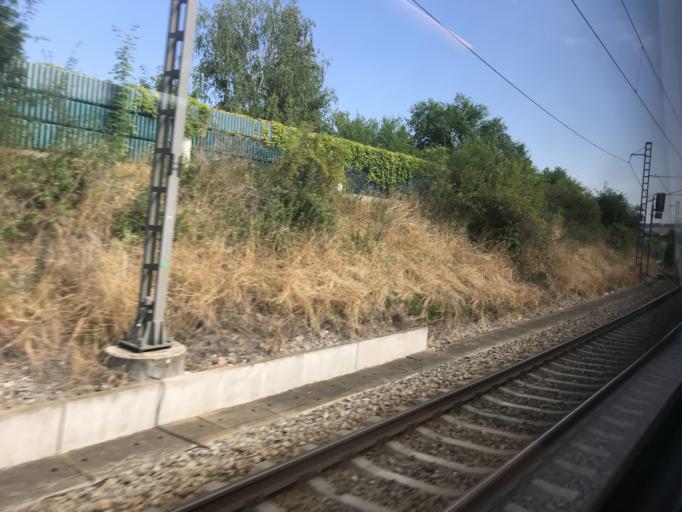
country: CZ
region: Central Bohemia
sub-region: Okres Benesov
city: Benesov
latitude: 49.7902
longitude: 14.6939
